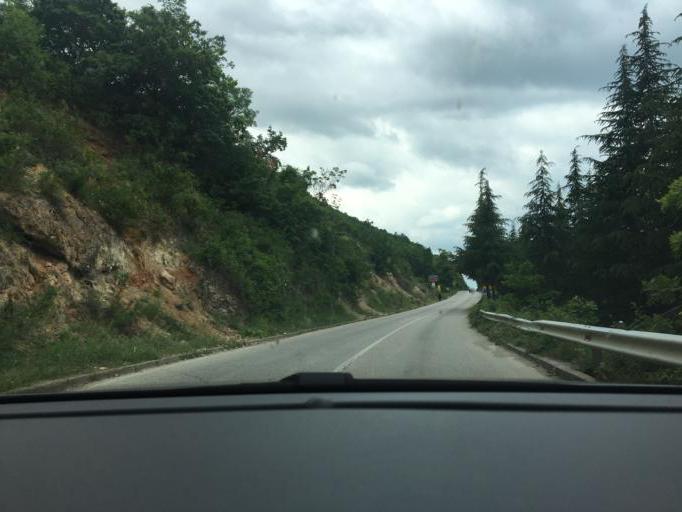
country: MK
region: Ohrid
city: Ohrid
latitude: 41.0596
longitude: 20.8032
